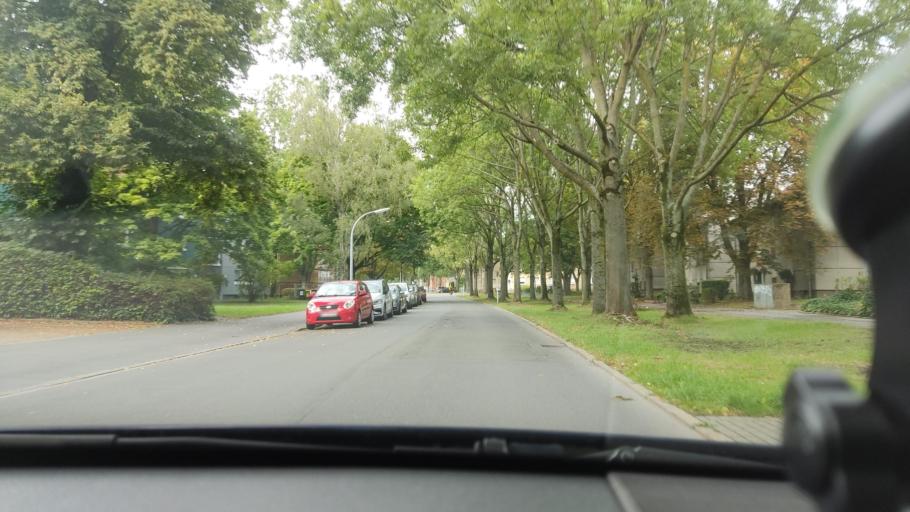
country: DE
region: North Rhine-Westphalia
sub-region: Regierungsbezirk Arnsberg
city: Dortmund
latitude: 51.5542
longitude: 7.4694
